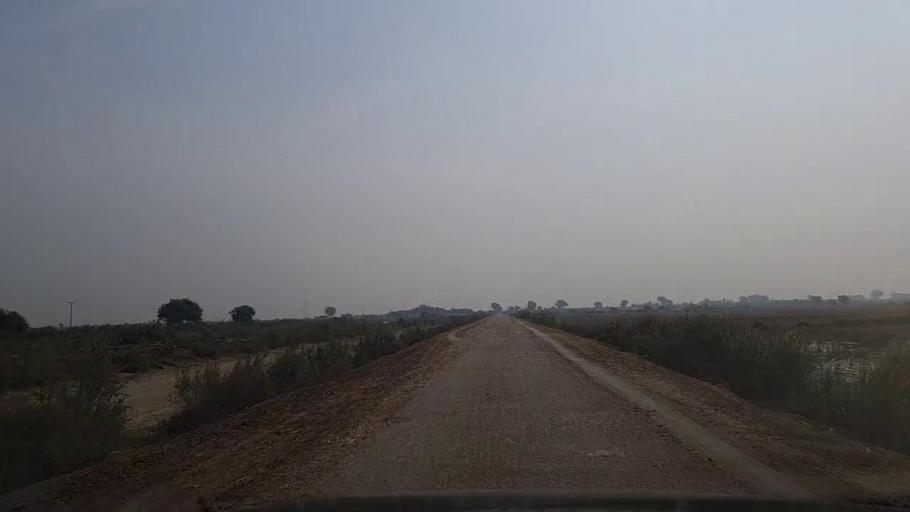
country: PK
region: Sindh
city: Mirpur Sakro
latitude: 24.3813
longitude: 67.7539
